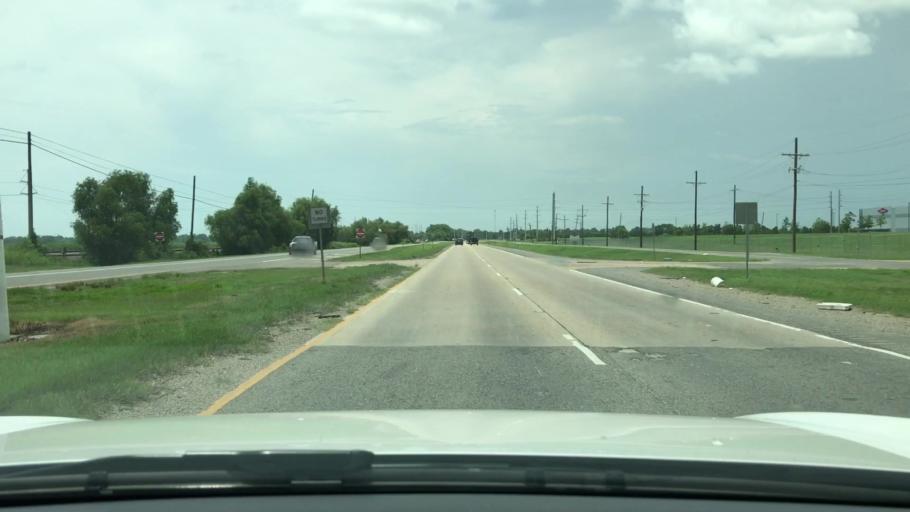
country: US
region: Louisiana
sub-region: West Baton Rouge Parish
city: Addis
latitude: 30.3338
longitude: -91.2576
